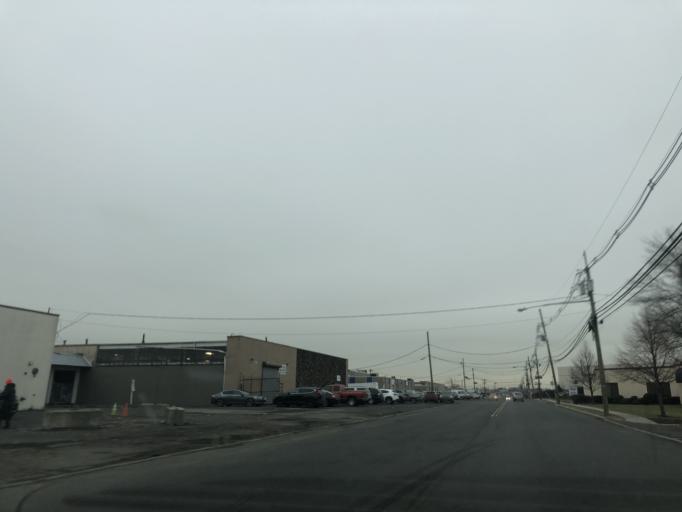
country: US
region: New Jersey
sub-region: Union County
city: Elizabeth
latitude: 40.6709
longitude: -74.1894
